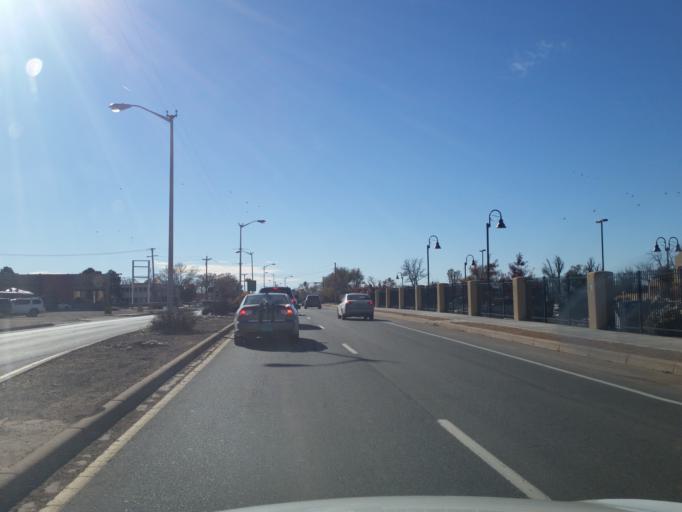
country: US
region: New Mexico
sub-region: Santa Fe County
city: Santa Fe
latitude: 35.6761
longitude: -105.9564
